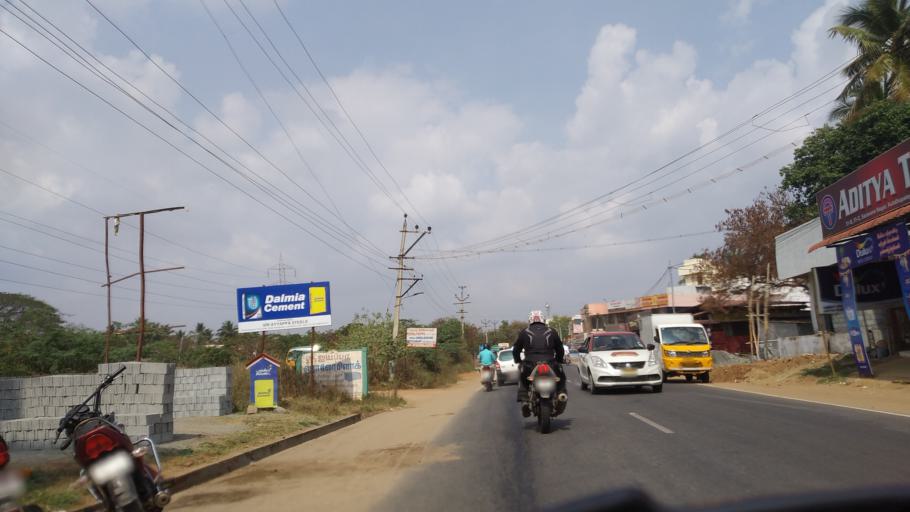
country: IN
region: Tamil Nadu
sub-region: Coimbatore
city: Perur
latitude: 10.9432
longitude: 76.9408
